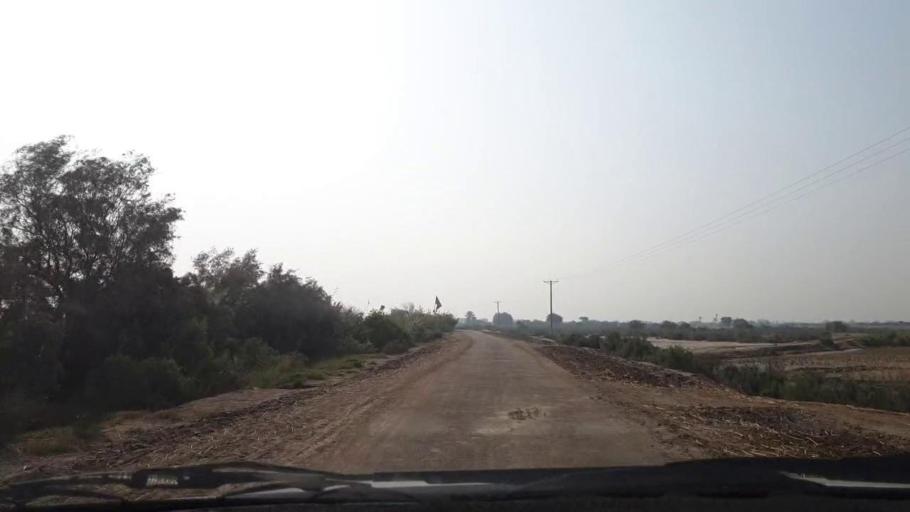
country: PK
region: Sindh
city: Tando Muhammad Khan
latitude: 25.0193
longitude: 68.4498
